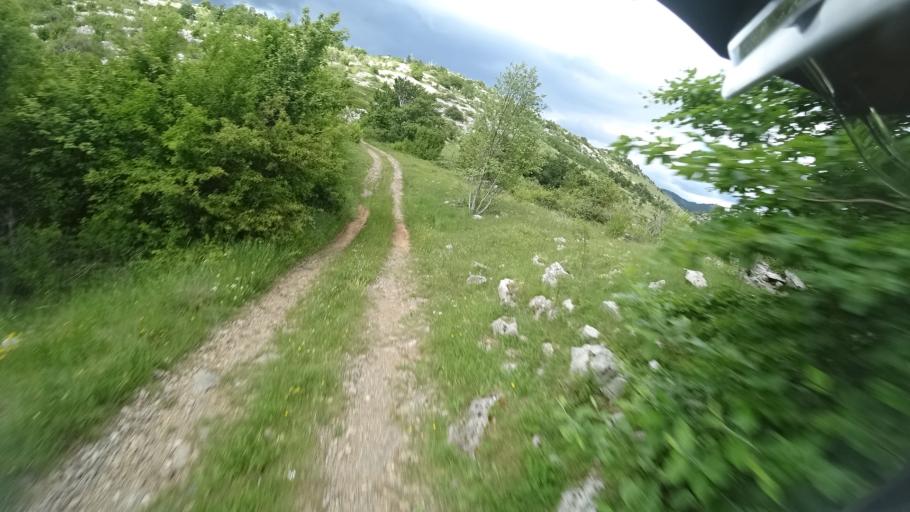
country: HR
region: Zadarska
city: Obrovac
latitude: 44.2680
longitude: 15.7389
